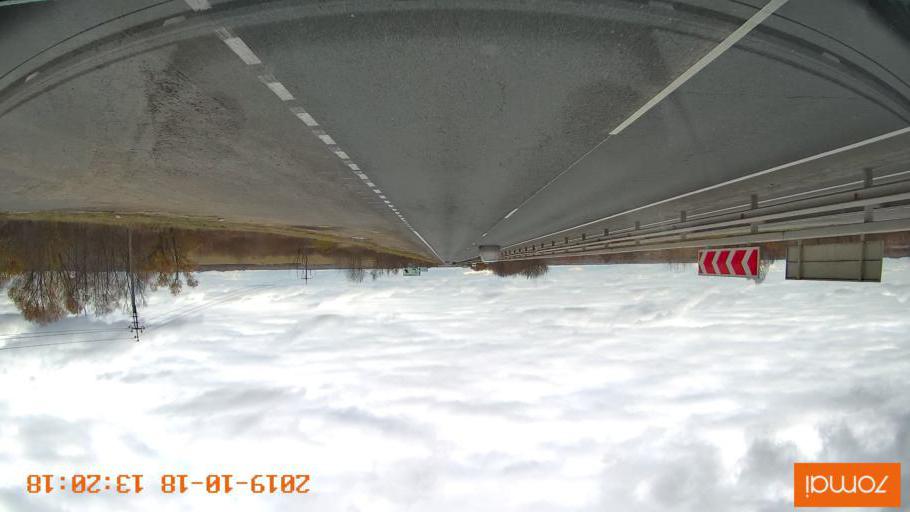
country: RU
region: Rjazan
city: Polyany
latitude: 54.6787
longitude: 39.8307
